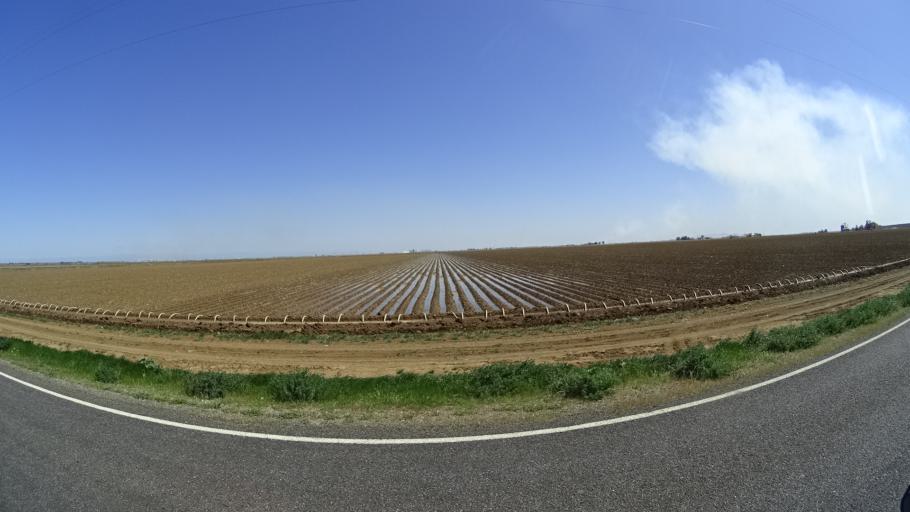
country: US
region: California
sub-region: Glenn County
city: Willows
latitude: 39.4639
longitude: -122.2489
